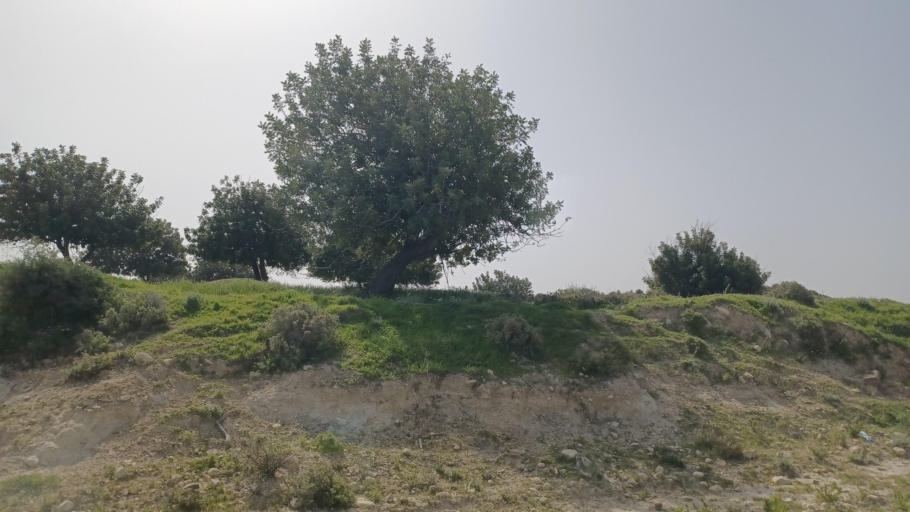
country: CY
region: Limassol
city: Pissouri
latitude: 34.6866
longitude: 32.7049
